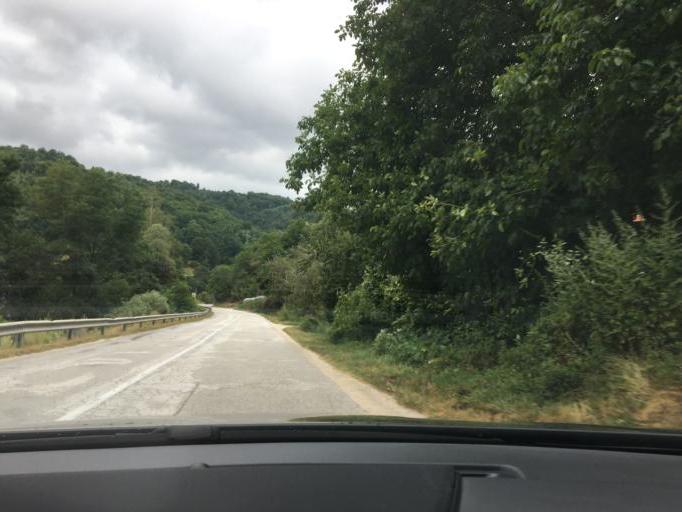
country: MK
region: Kriva Palanka
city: Kriva Palanka
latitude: 42.2247
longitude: 22.4003
